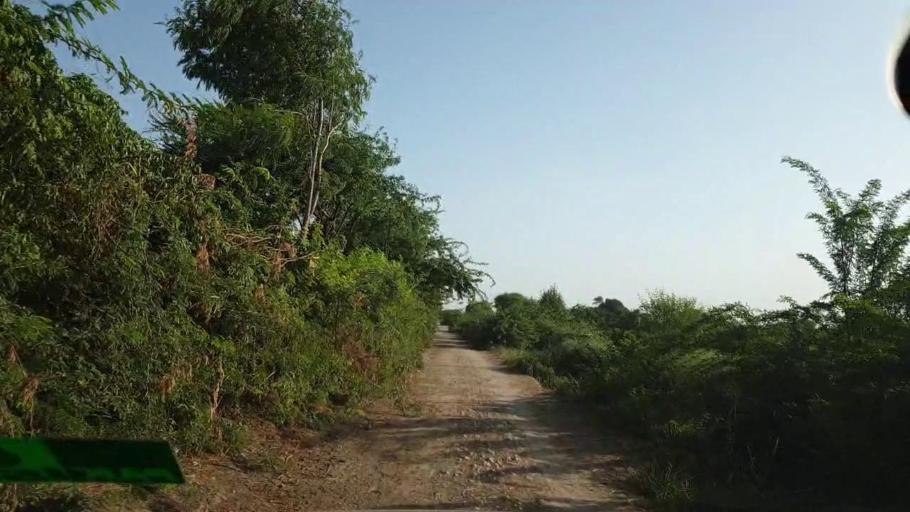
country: PK
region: Sindh
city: Naukot
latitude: 24.7286
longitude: 69.2517
